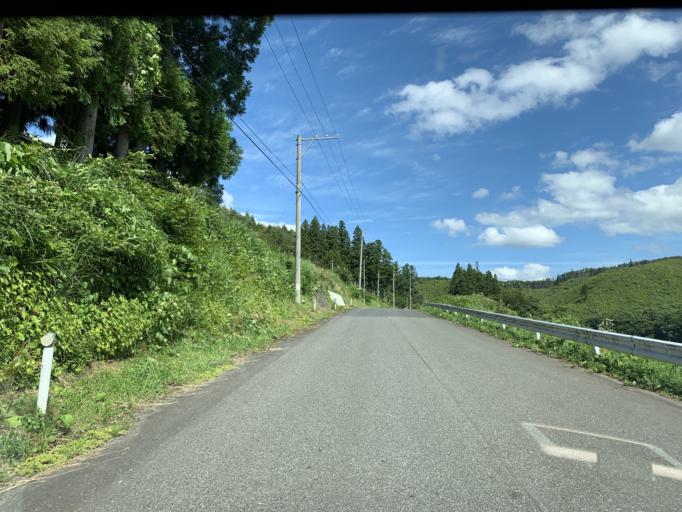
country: JP
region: Iwate
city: Ichinoseki
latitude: 38.9632
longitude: 140.9552
